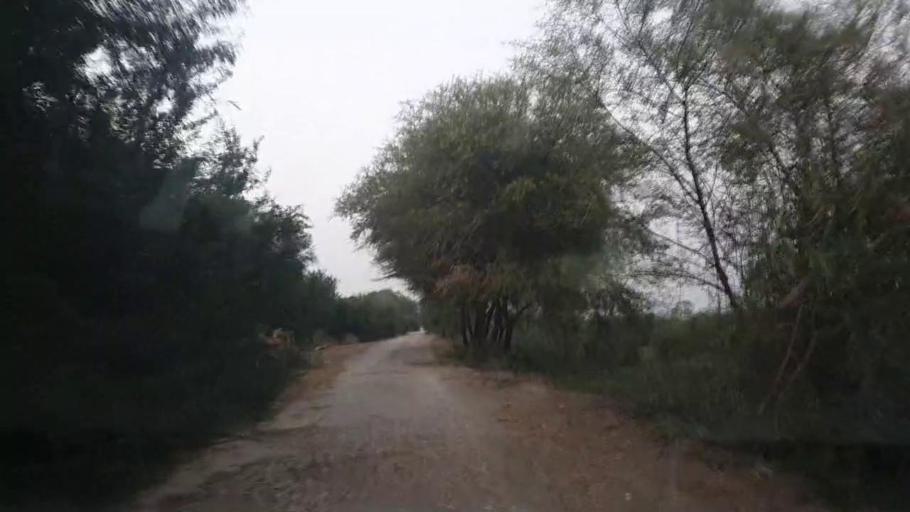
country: PK
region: Sindh
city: Mirpur Sakro
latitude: 24.5832
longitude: 67.7847
